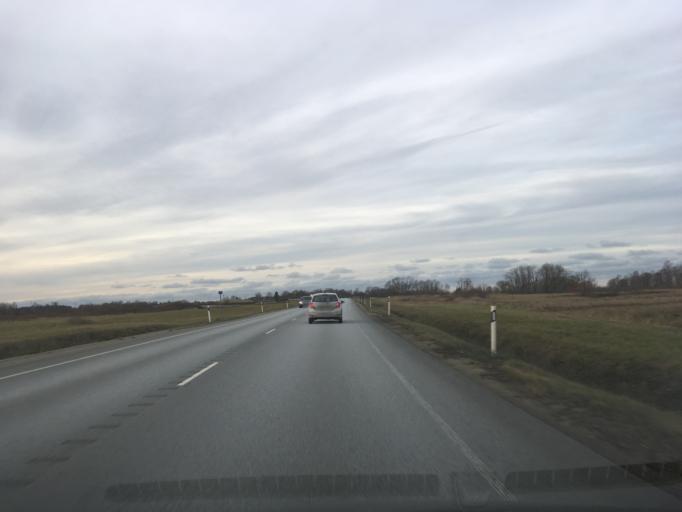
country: EE
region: Ida-Virumaa
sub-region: Kivioli linn
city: Kivioli
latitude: 59.4236
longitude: 26.9650
